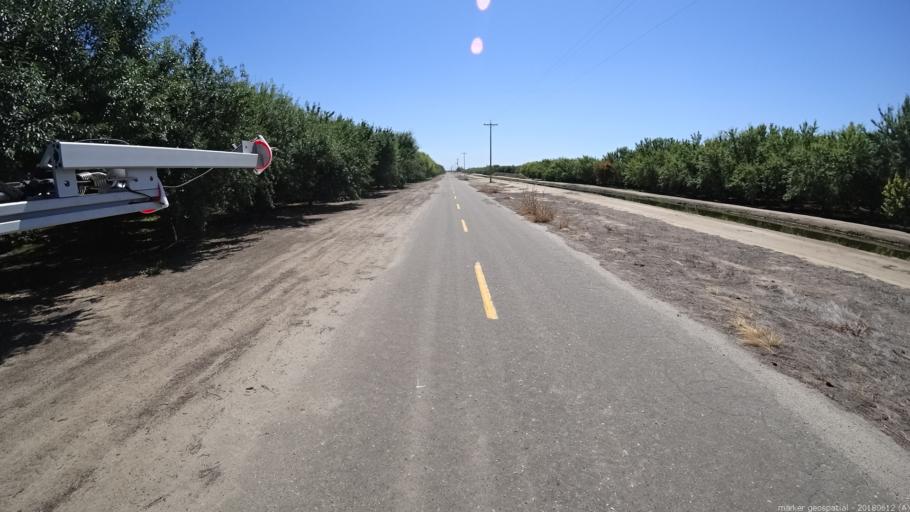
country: US
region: California
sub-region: Madera County
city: Chowchilla
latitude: 37.0255
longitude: -120.2865
